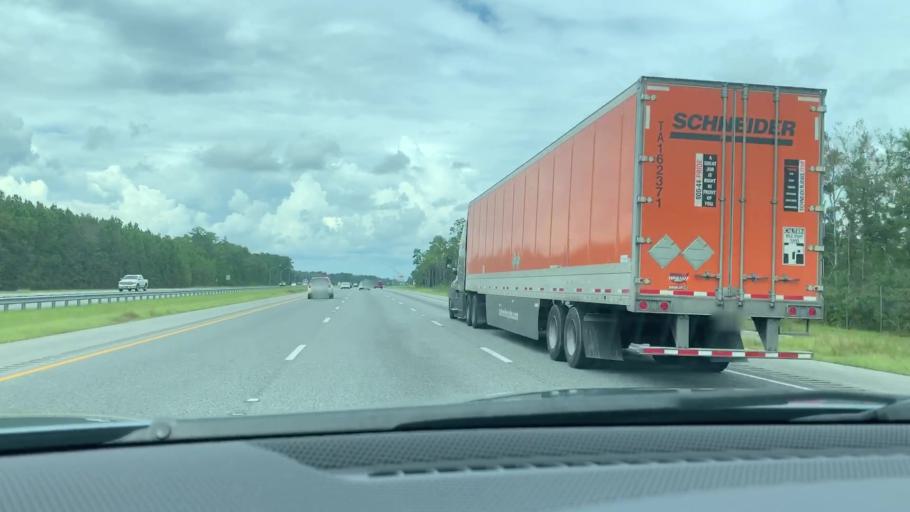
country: US
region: Georgia
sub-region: McIntosh County
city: Darien
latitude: 31.4684
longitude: -81.4466
